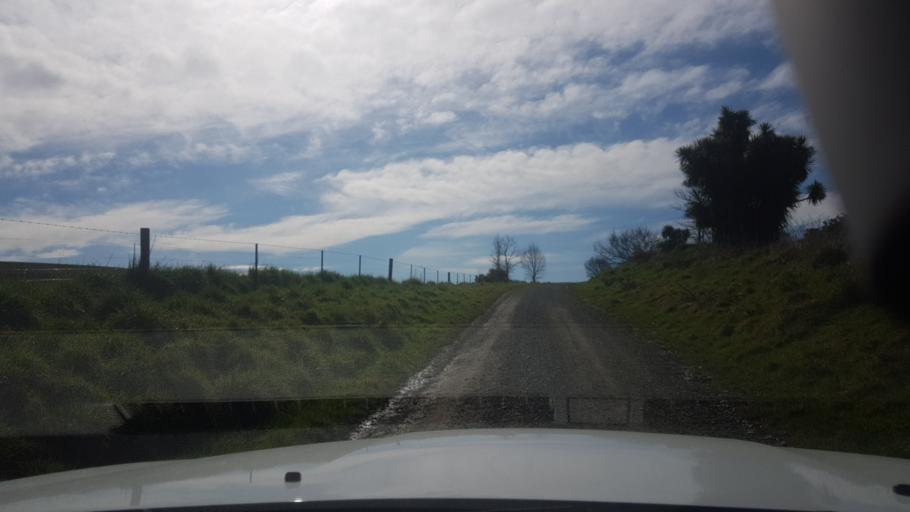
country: NZ
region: Canterbury
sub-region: Timaru District
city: Pleasant Point
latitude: -44.2001
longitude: 171.1871
